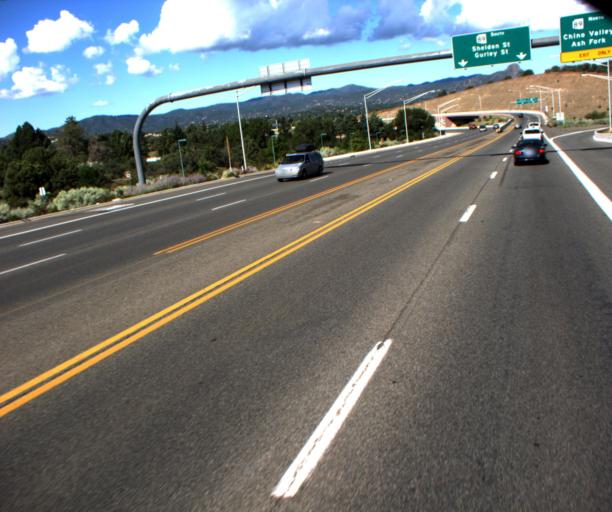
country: US
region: Arizona
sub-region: Yavapai County
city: Prescott
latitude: 34.5483
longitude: -112.4458
